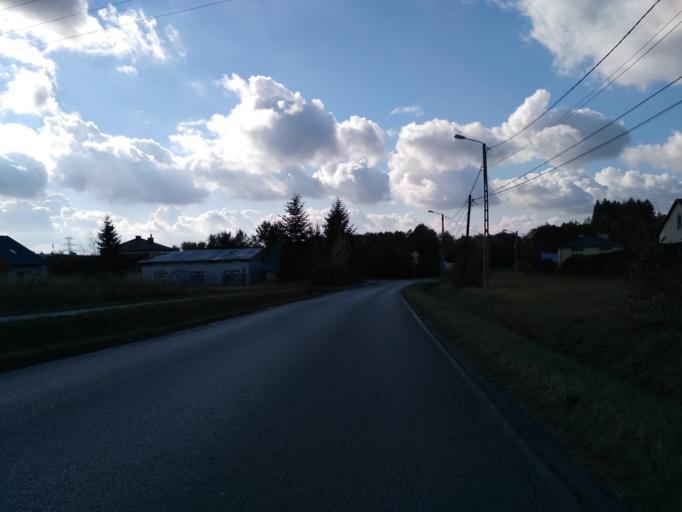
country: PL
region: Subcarpathian Voivodeship
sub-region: Powiat rzeszowski
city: Glogow Malopolski
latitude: 50.1447
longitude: 21.9491
